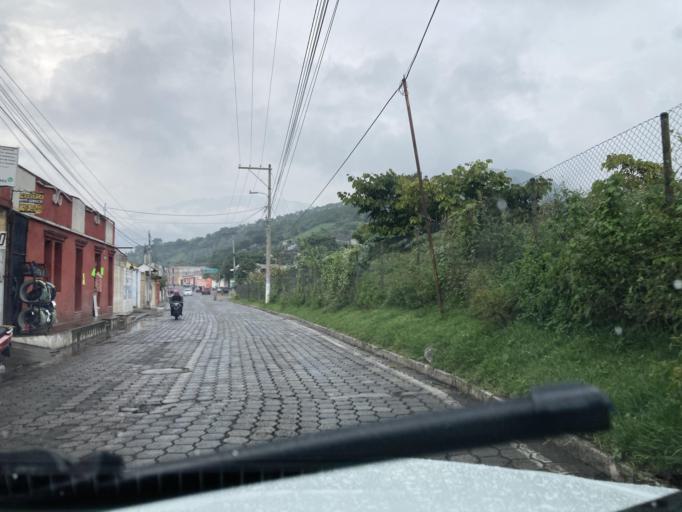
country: GT
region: Sacatepequez
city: San Miguel Duenas
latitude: 14.5234
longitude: -90.7935
